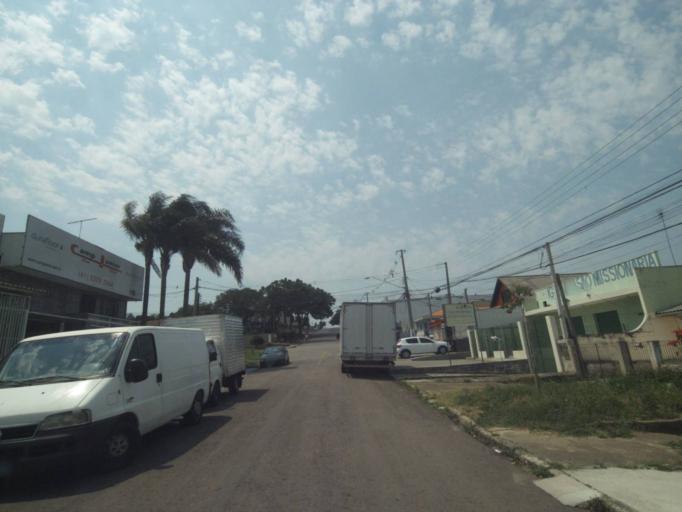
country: BR
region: Parana
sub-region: Sao Jose Dos Pinhais
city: Sao Jose dos Pinhais
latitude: -25.5367
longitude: -49.2485
